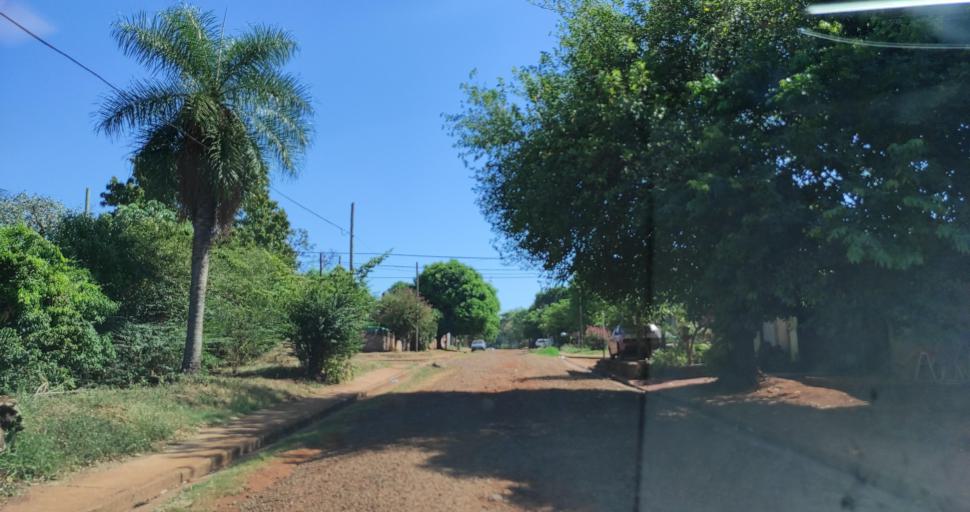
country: AR
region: Misiones
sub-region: Departamento de Capital
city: Posadas
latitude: -27.3895
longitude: -55.9330
